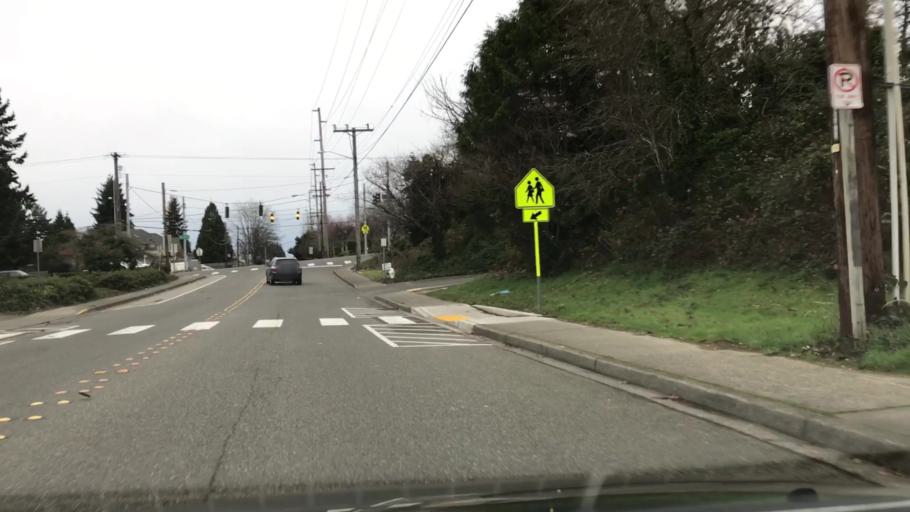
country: US
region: Washington
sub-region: King County
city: Kent
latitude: 47.3861
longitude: -122.2074
